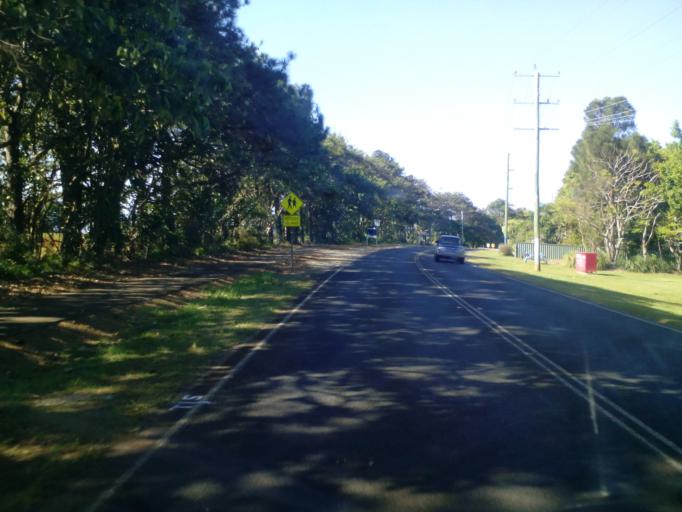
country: AU
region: New South Wales
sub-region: Tweed
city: Kingscliff
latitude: -28.2647
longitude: 153.5674
